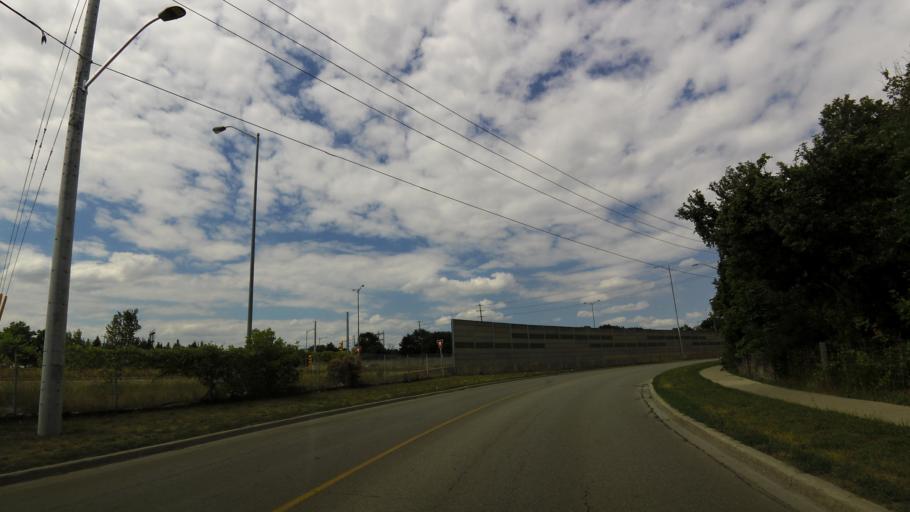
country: CA
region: Ontario
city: Etobicoke
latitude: 43.5835
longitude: -79.5819
